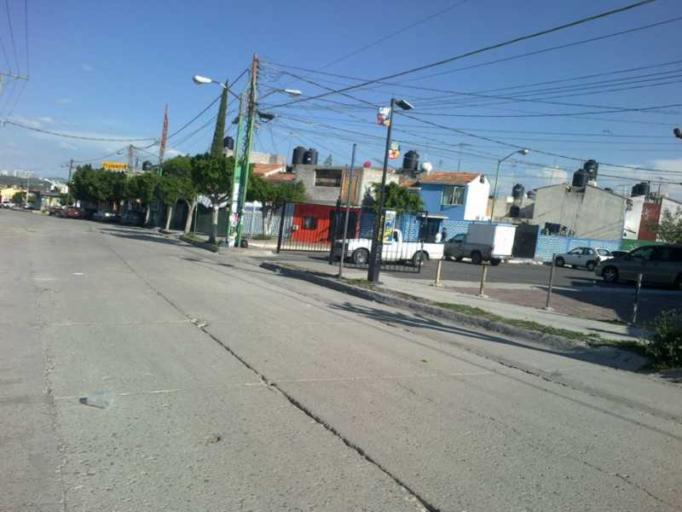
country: MX
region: Queretaro
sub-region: Queretaro
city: Sergio Villasenor
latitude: 20.6287
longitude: -100.4079
